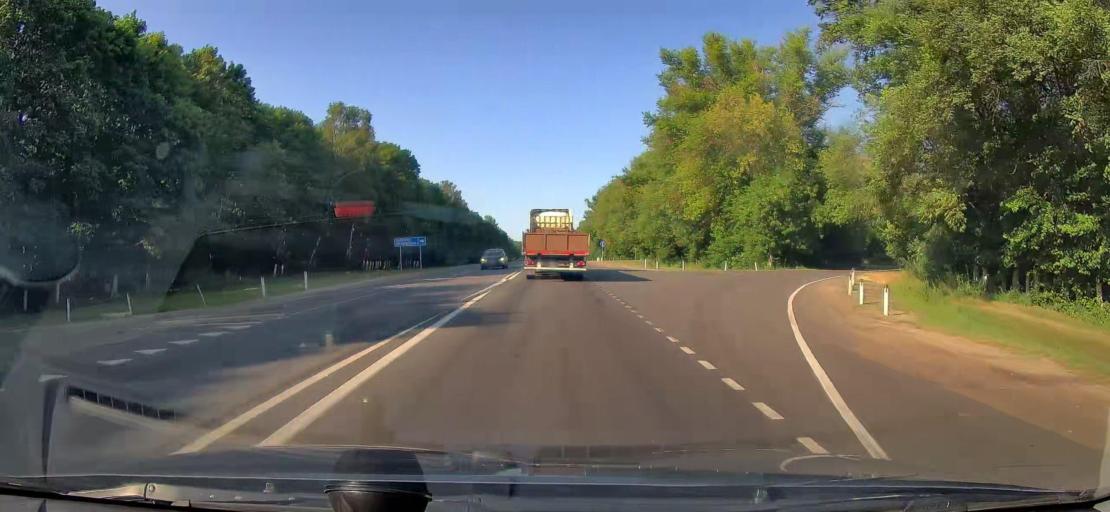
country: RU
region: Orjol
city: Mtsensk
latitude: 53.1932
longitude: 36.4278
